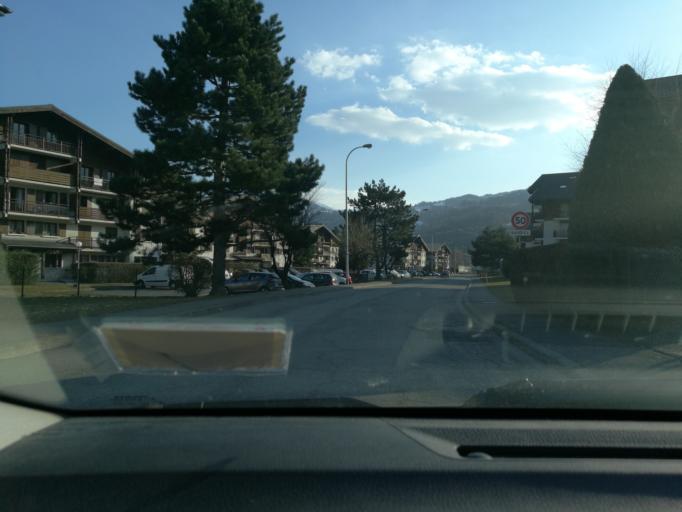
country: FR
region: Rhone-Alpes
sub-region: Departement de la Haute-Savoie
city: Sallanches
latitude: 45.9361
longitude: 6.6389
